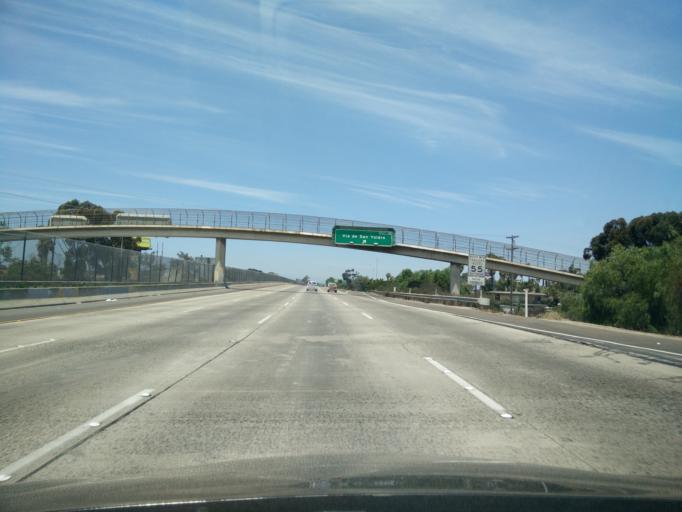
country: MX
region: Baja California
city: Tijuana
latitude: 32.5500
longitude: -117.0412
